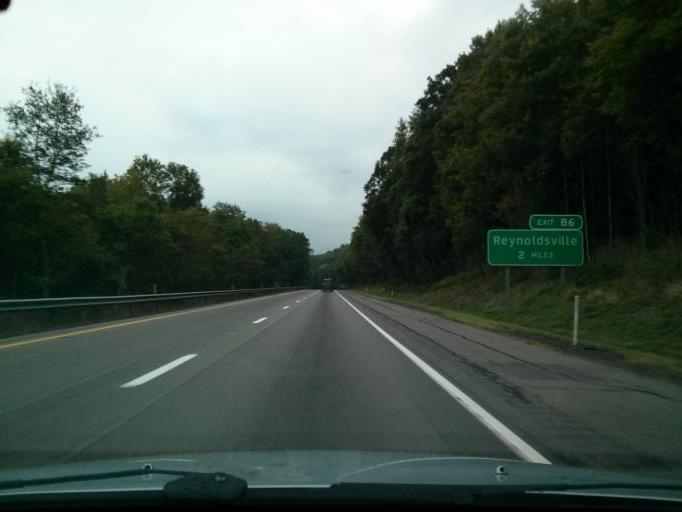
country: US
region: Pennsylvania
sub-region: Jefferson County
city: Brookville
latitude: 41.1543
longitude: -78.9998
